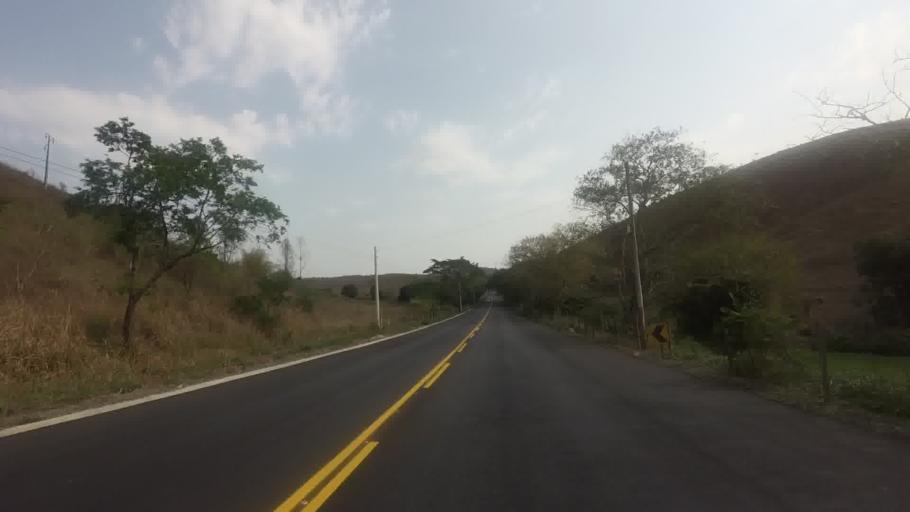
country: BR
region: Rio de Janeiro
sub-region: Bom Jesus Do Itabapoana
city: Bom Jesus do Itabapoana
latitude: -21.2427
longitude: -41.7559
